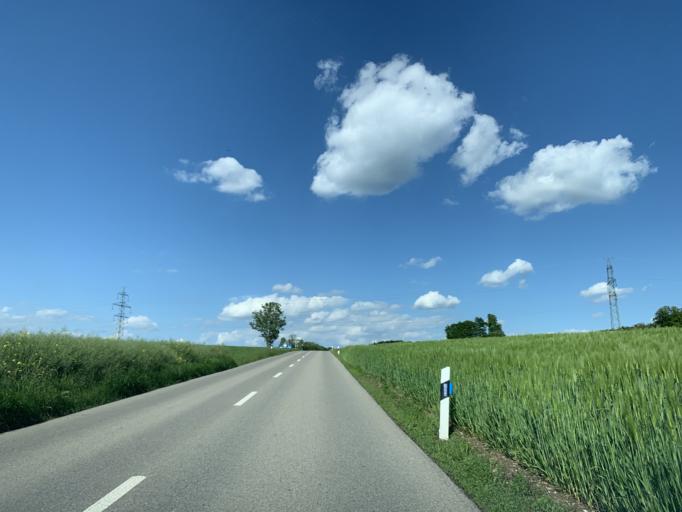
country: CH
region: Zurich
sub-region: Bezirk Pfaeffikon
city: Effretikon / Watt
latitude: 47.4406
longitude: 8.7190
